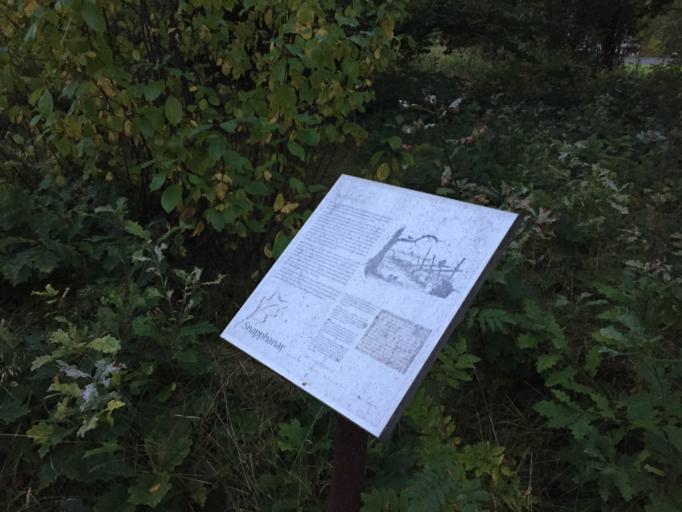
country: SE
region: Skane
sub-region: Osby Kommun
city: Osby
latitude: 56.3514
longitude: 13.9677
